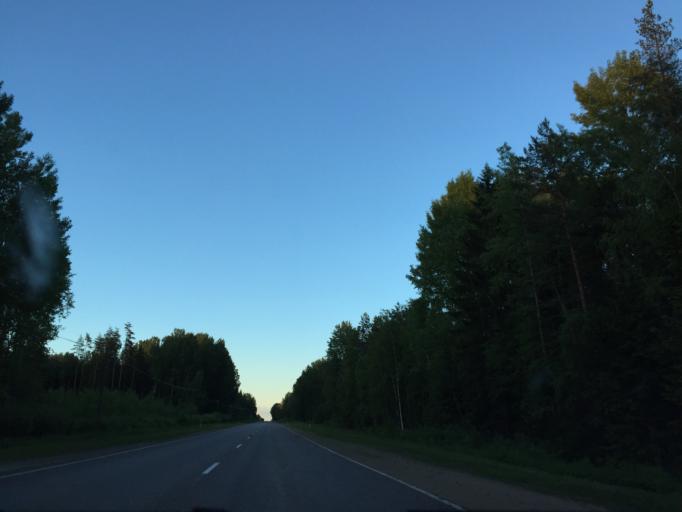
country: LV
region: Smiltene
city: Smiltene
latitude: 57.3929
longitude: 25.9937
